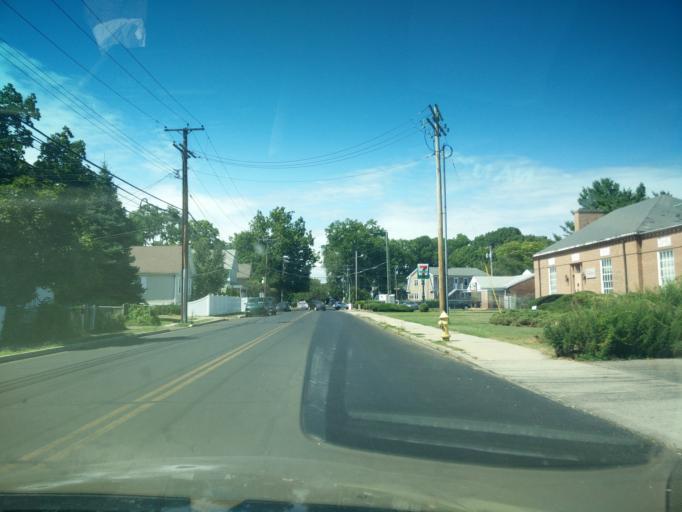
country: US
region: Connecticut
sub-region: Fairfield County
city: Fairfield
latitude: 41.1371
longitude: -73.2547
